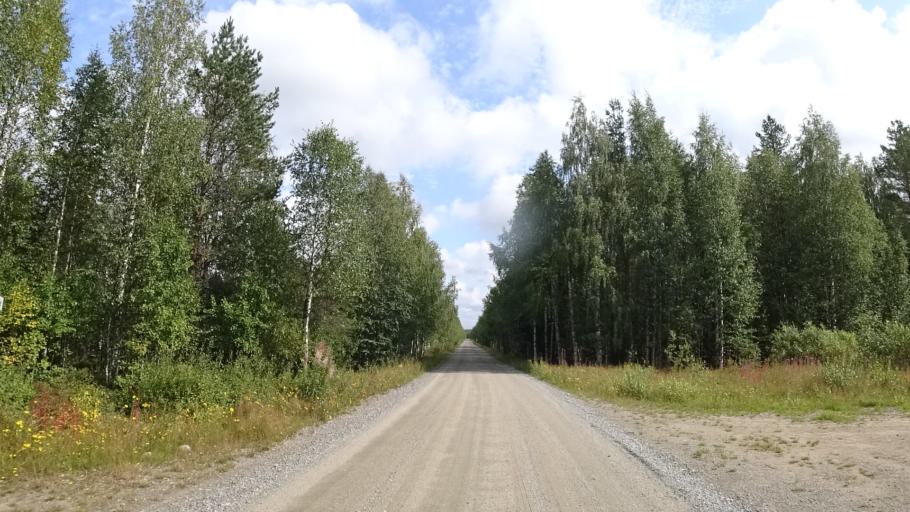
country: FI
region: North Karelia
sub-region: Joensuu
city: Ilomantsi
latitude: 62.9264
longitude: 31.3894
